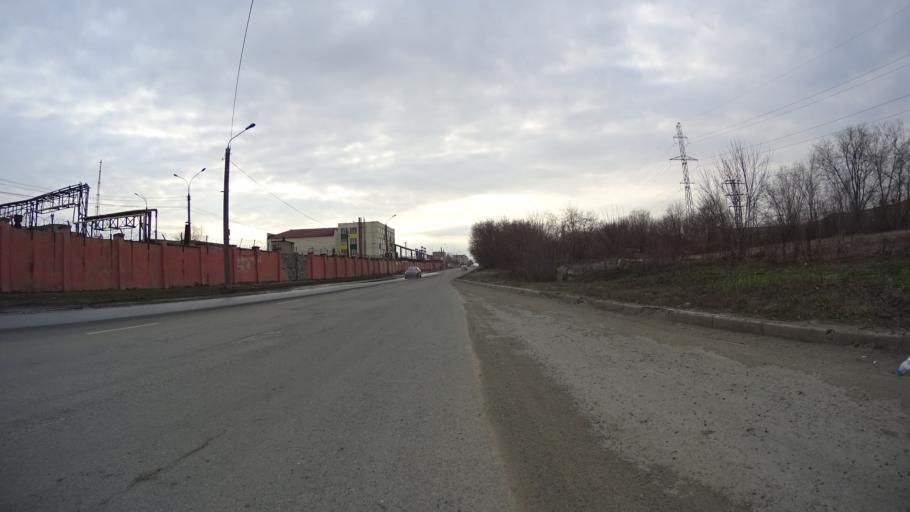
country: RU
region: Chelyabinsk
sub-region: Gorod Chelyabinsk
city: Chelyabinsk
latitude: 55.1584
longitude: 61.4807
